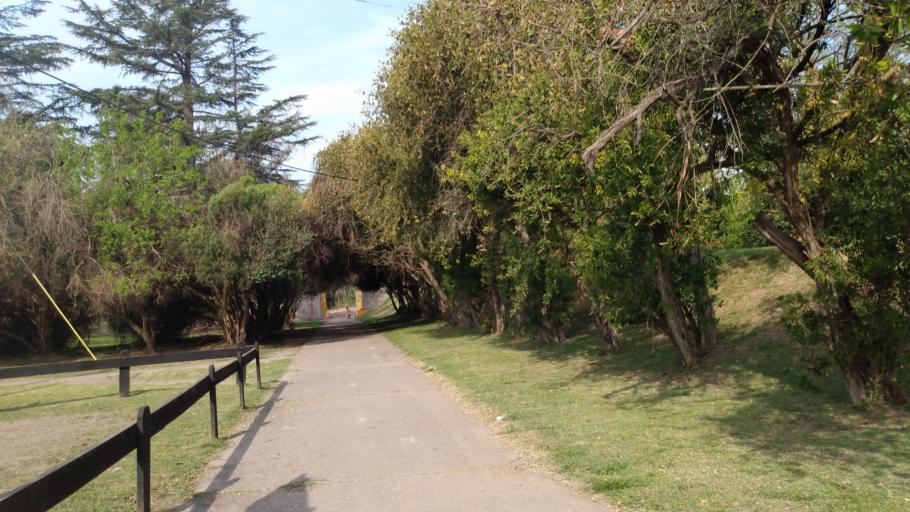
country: AR
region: Buenos Aires
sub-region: Partido de Lujan
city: Lujan
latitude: -34.5901
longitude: -59.1841
